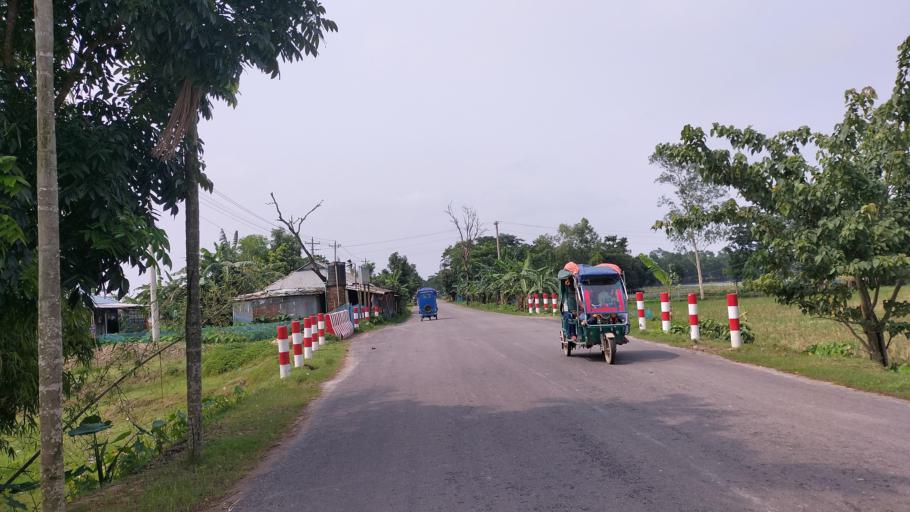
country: BD
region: Dhaka
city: Netrakona
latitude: 24.9486
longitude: 90.8320
